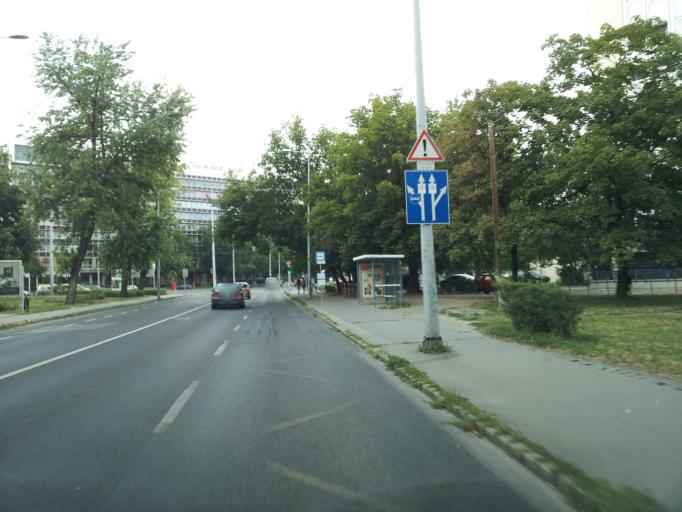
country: HU
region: Budapest
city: Budapest XI. keruelet
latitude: 47.4724
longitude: 19.0525
